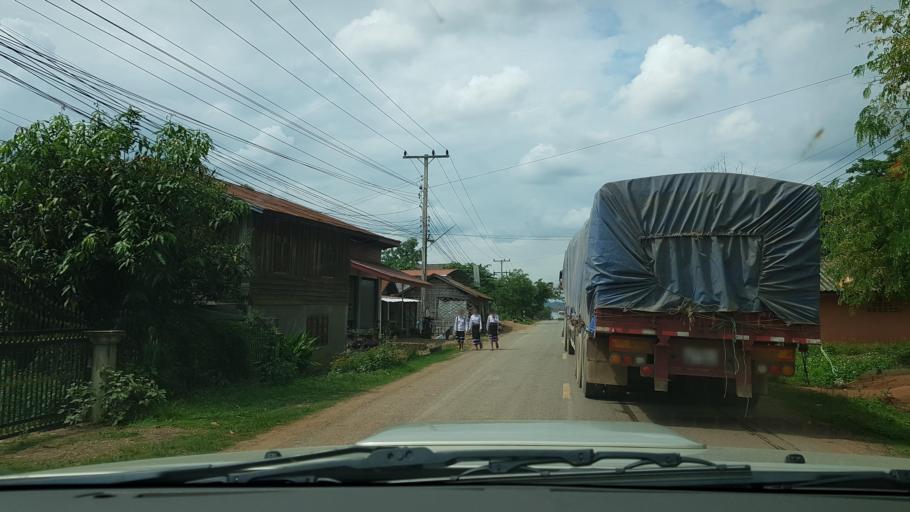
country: LA
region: Loungnamtha
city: Muang Nale
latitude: 20.2915
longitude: 101.6330
